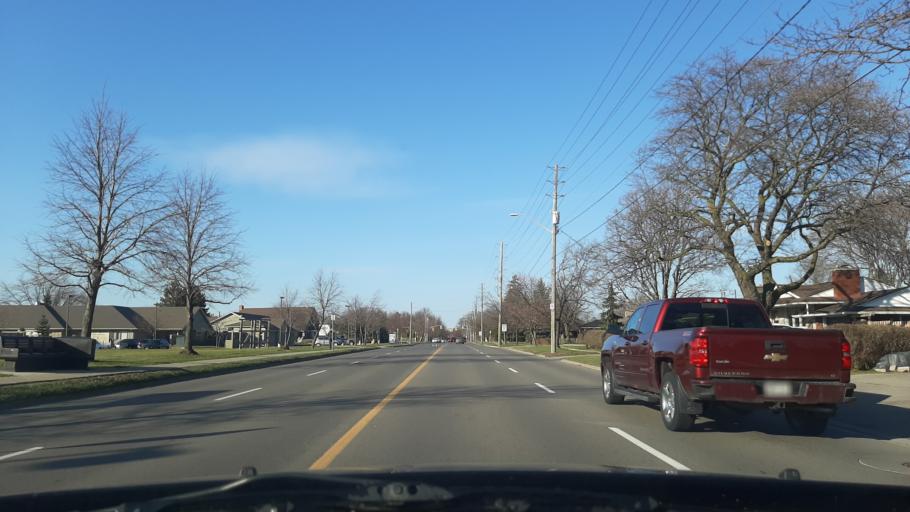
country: CA
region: Ontario
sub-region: Regional Municipality of Niagara
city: St. Catharines
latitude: 43.1833
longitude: -79.2661
